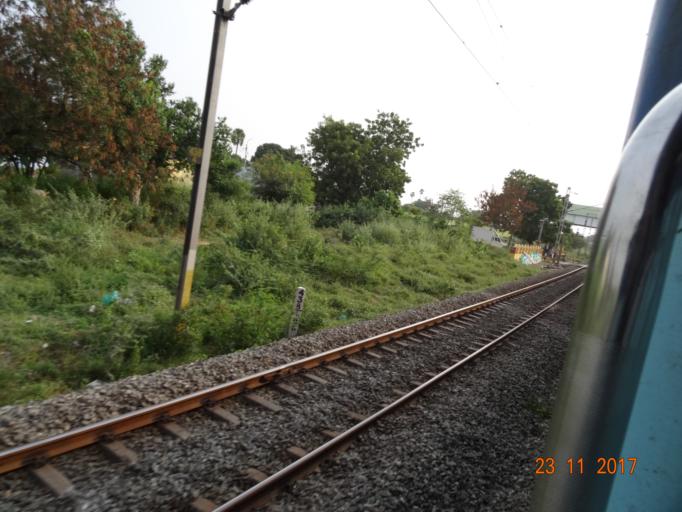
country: IN
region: Tamil Nadu
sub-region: Tiruppur
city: Tiruppur
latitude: 11.1294
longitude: 77.3701
